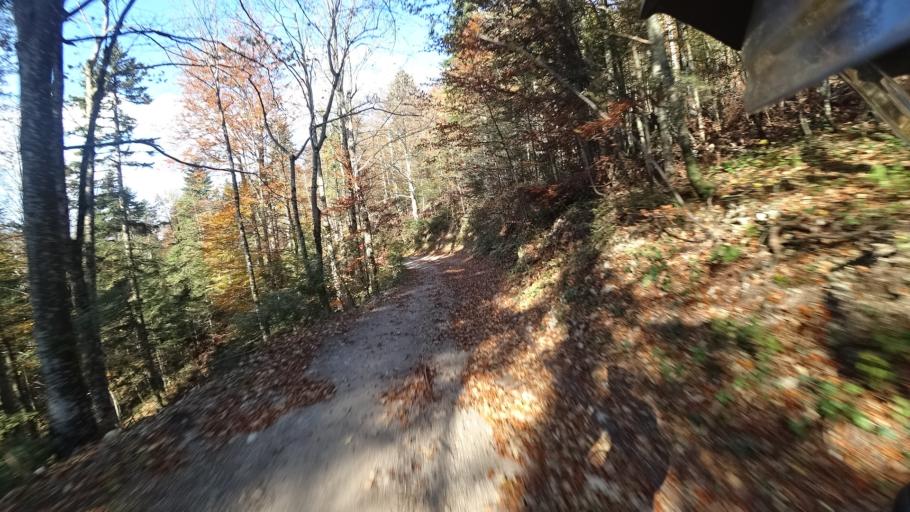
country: HR
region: Karlovacka
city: Plaski
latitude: 45.0314
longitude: 15.3599
